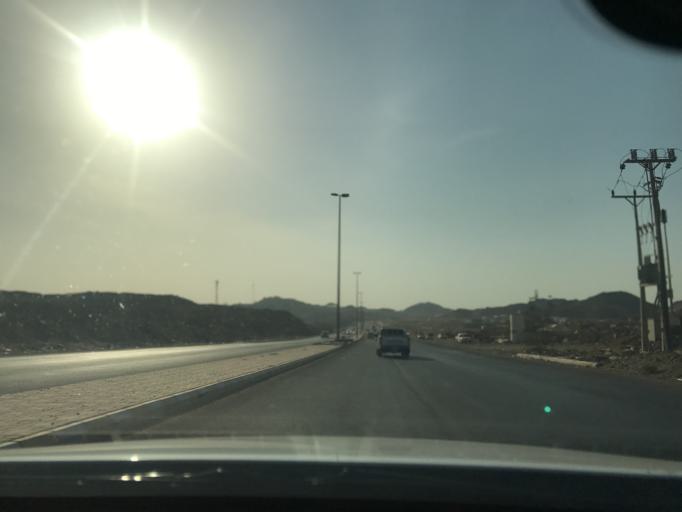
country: SA
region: Makkah
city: Jeddah
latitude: 21.4131
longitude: 39.4186
